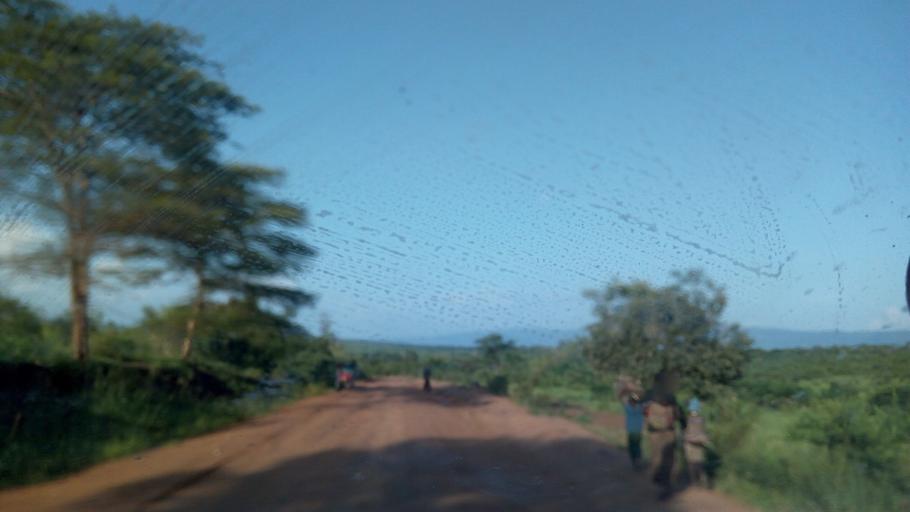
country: BI
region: Bururi
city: Rumonge
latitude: -4.2000
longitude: 29.0252
